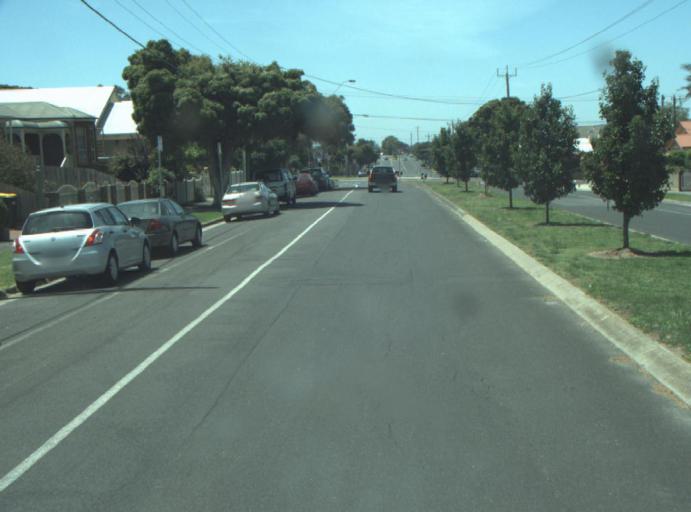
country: AU
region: Victoria
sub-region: Greater Geelong
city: East Geelong
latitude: -38.1573
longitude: 144.3633
